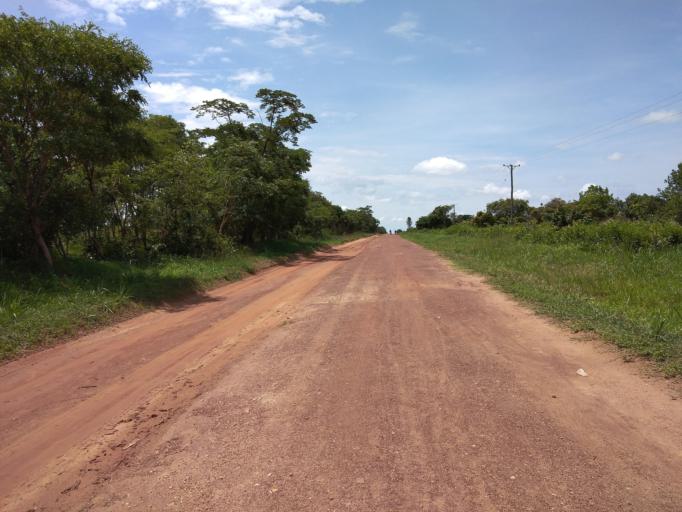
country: ZM
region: Copperbelt
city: Luanshya
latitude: -13.4793
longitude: 28.6812
